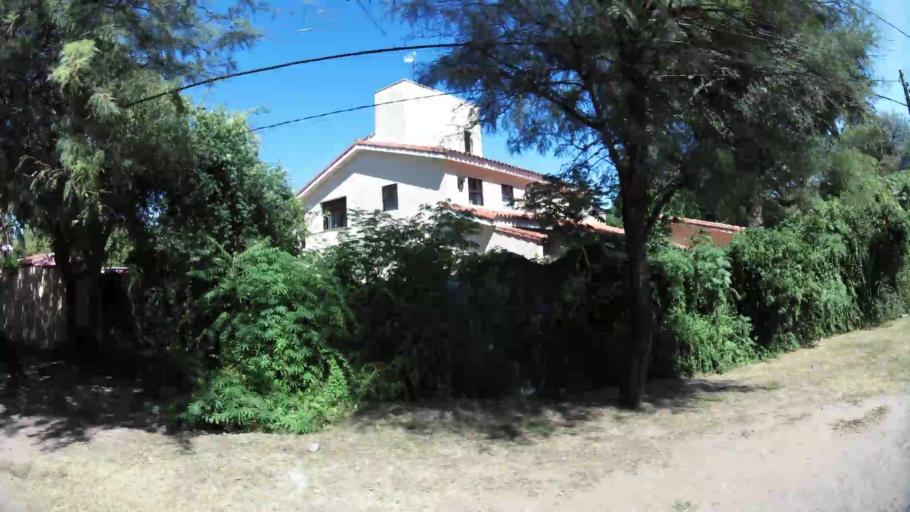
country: AR
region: Cordoba
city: Villa Allende
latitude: -31.2932
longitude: -64.2866
